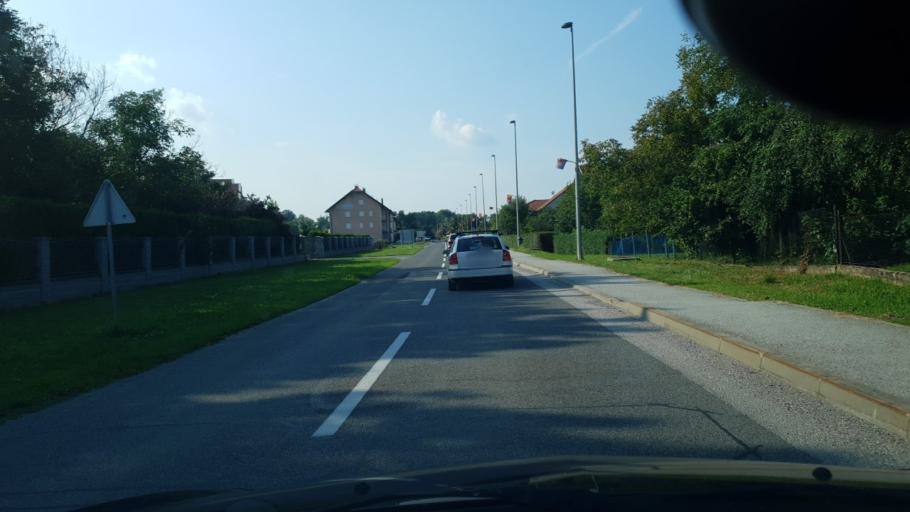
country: HR
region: Krapinsko-Zagorska
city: Oroslavje
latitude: 45.9908
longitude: 15.9159
